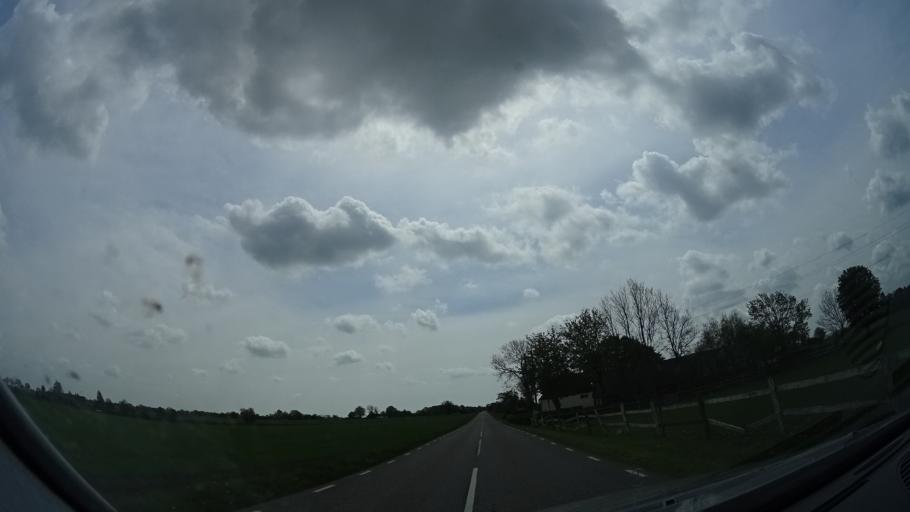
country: SE
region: Skane
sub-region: Hoors Kommun
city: Loberod
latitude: 55.7510
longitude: 13.4869
